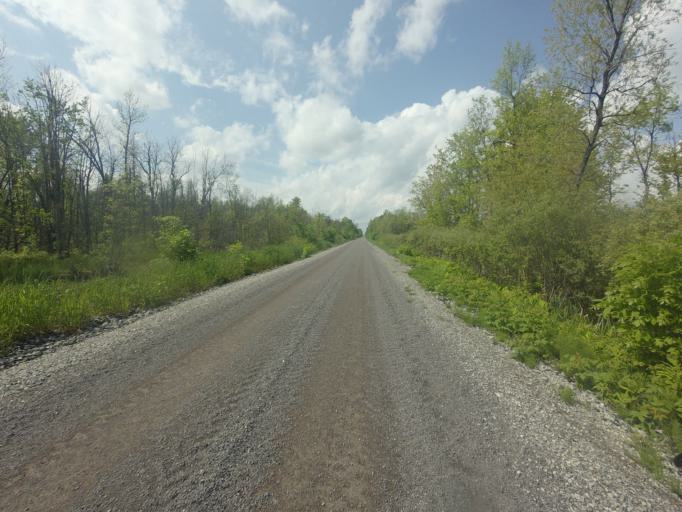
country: CA
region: Ontario
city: Carleton Place
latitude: 45.0412
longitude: -76.0849
